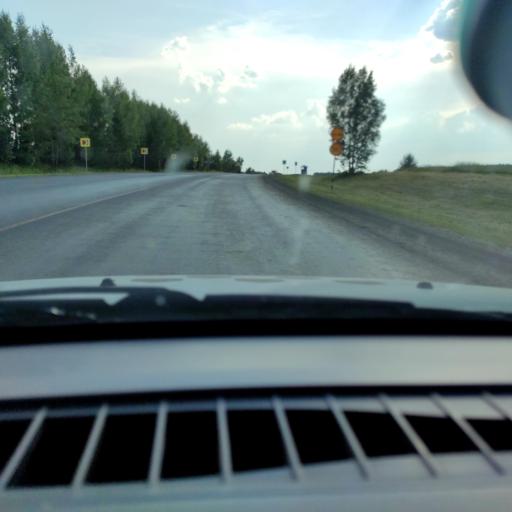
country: RU
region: Udmurtiya
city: Debesy
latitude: 57.7041
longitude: 54.0682
